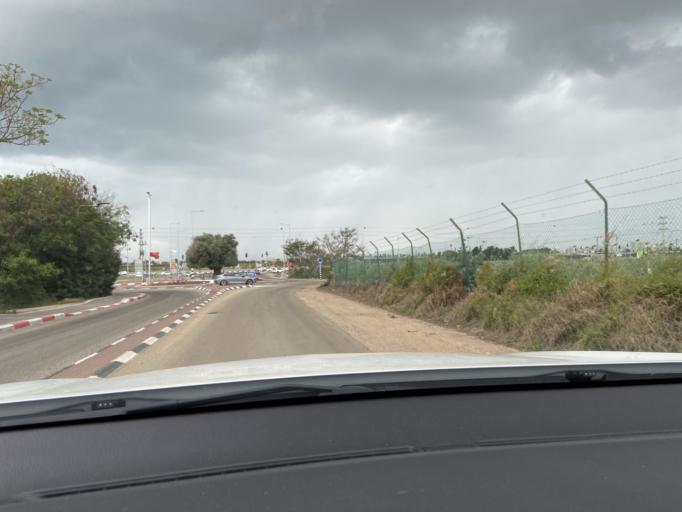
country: IL
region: Northern District
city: El Mazra`a
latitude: 32.9778
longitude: 35.0958
